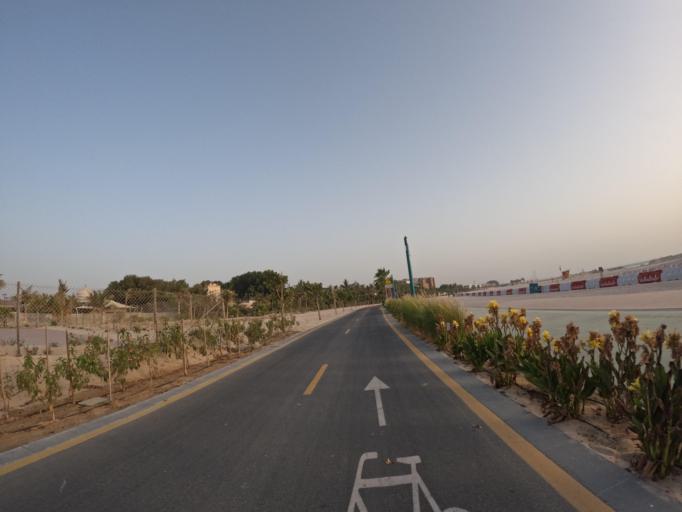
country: AE
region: Dubai
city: Dubai
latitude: 25.1900
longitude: 55.2277
